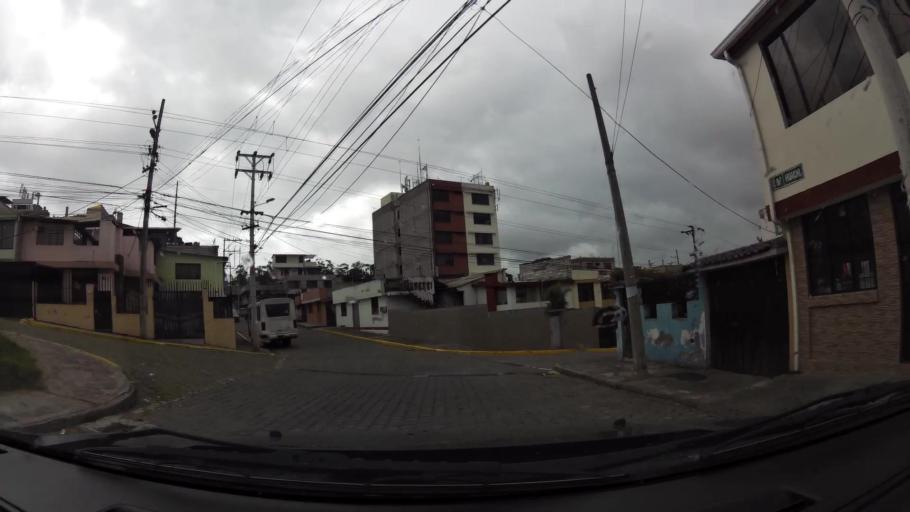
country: EC
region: Pichincha
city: Quito
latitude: -0.1163
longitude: -78.5010
